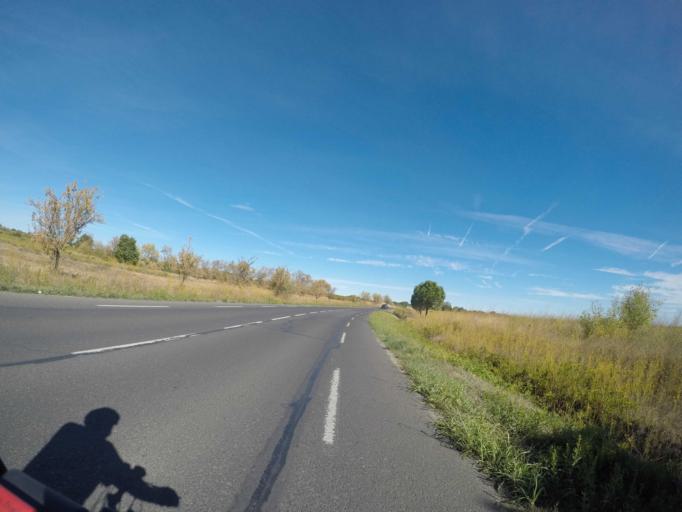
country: FR
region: Languedoc-Roussillon
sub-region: Departement des Pyrenees-Orientales
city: Ponteilla
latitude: 42.6190
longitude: 2.8111
